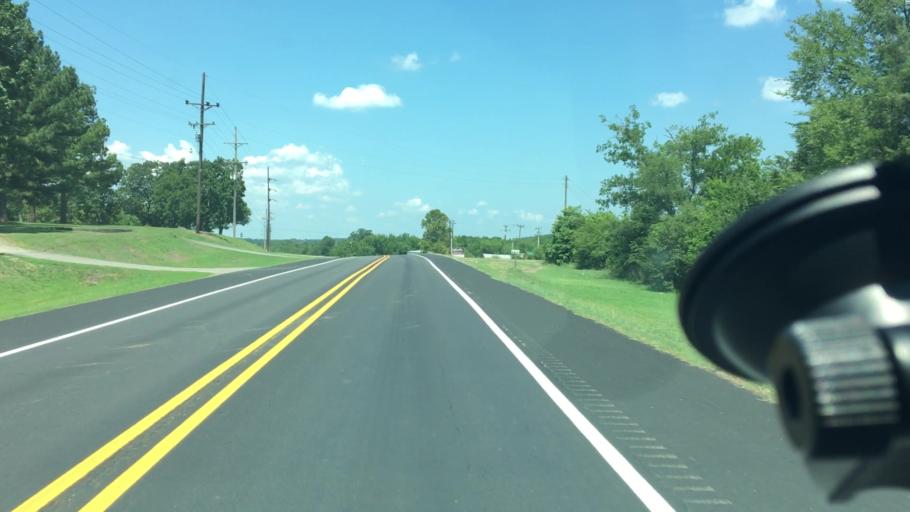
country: US
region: Arkansas
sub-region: Sebastian County
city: Lavaca
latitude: 35.3037
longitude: -94.1675
